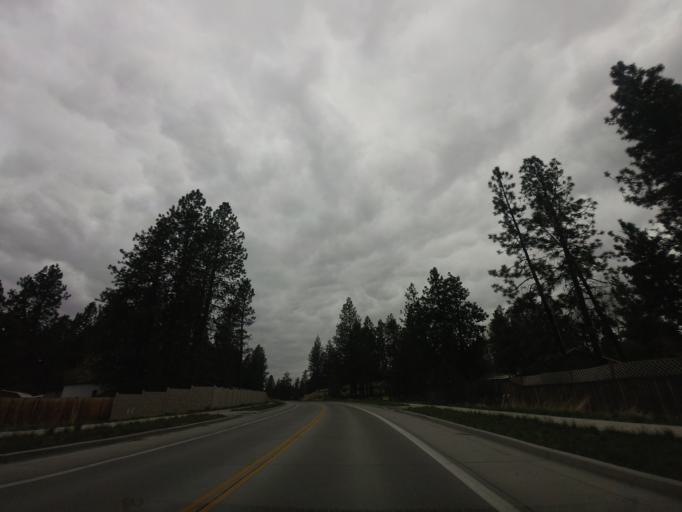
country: US
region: Oregon
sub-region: Deschutes County
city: Bend
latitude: 44.0190
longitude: -121.3249
